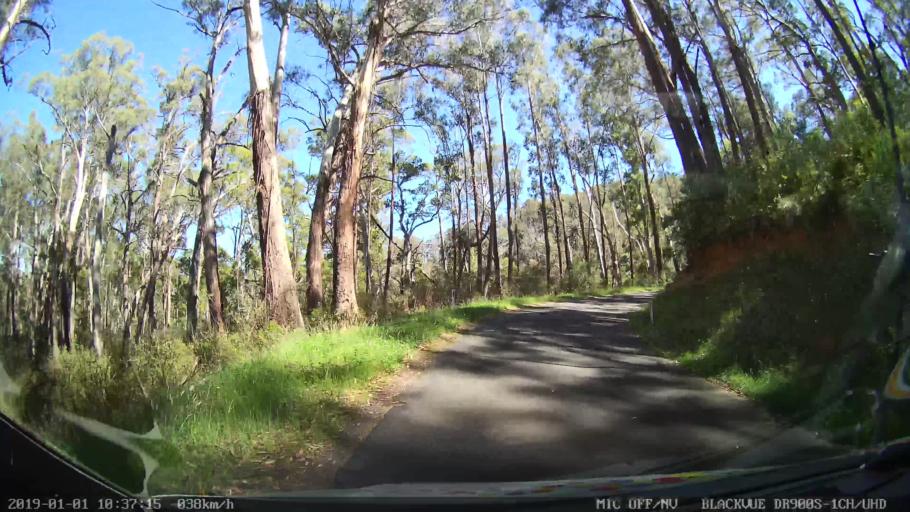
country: AU
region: New South Wales
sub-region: Snowy River
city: Jindabyne
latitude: -36.0495
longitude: 148.3038
